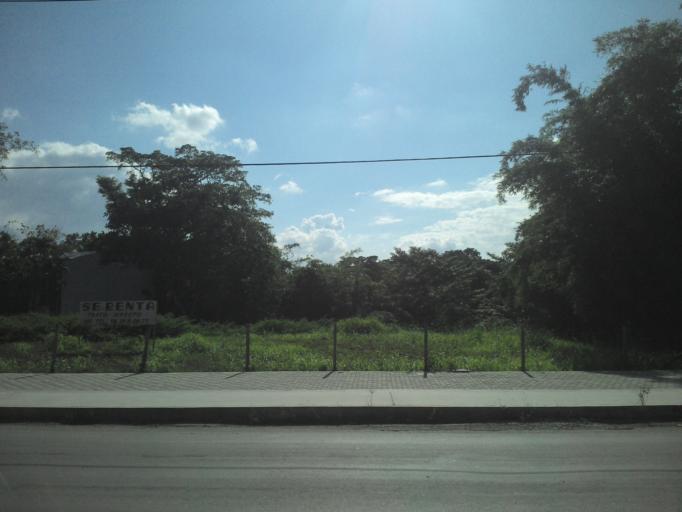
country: MX
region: Chiapas
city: Palenque
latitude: 17.5142
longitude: -91.9925
